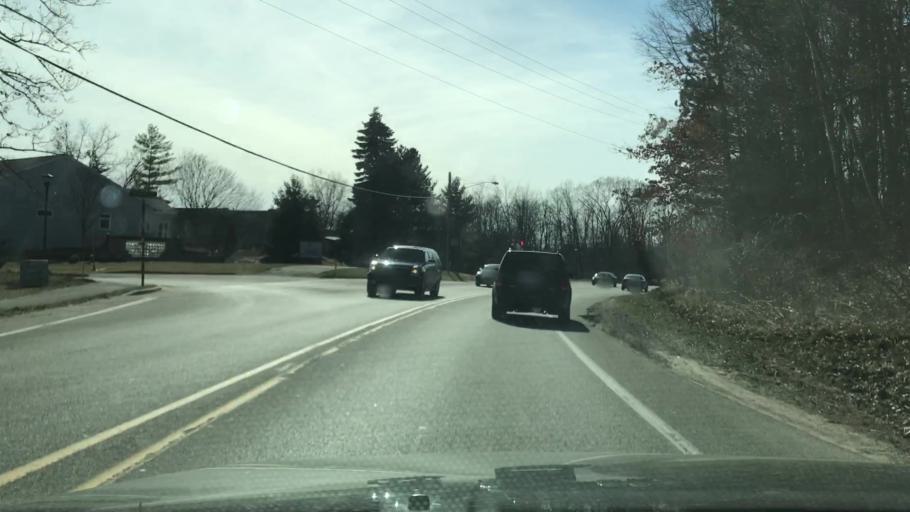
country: US
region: Michigan
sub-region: Kent County
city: Forest Hills
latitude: 42.9203
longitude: -85.5409
